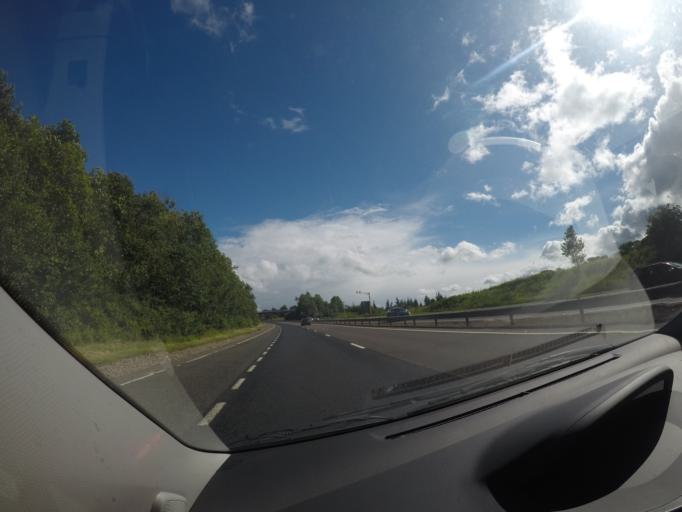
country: GB
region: Scotland
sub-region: Stirling
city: Dunblane
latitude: 56.1863
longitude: -3.9857
